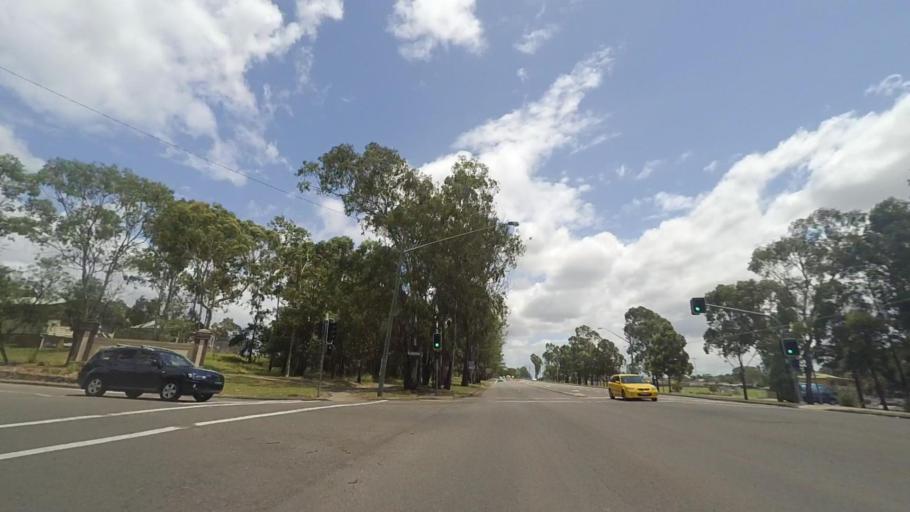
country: AU
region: New South Wales
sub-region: Liverpool
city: Holsworthy
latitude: -33.9558
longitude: 150.9556
